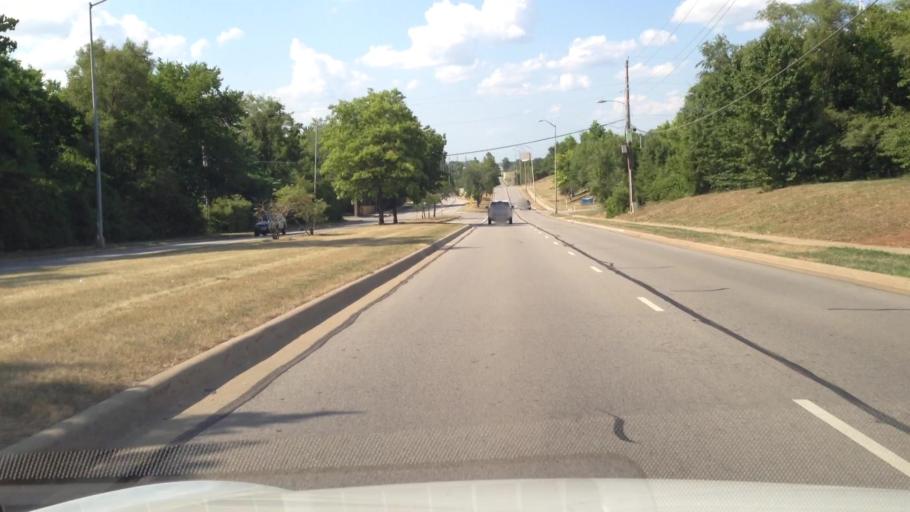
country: US
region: Kansas
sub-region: Johnson County
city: Olathe
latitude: 38.9187
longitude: -94.7973
